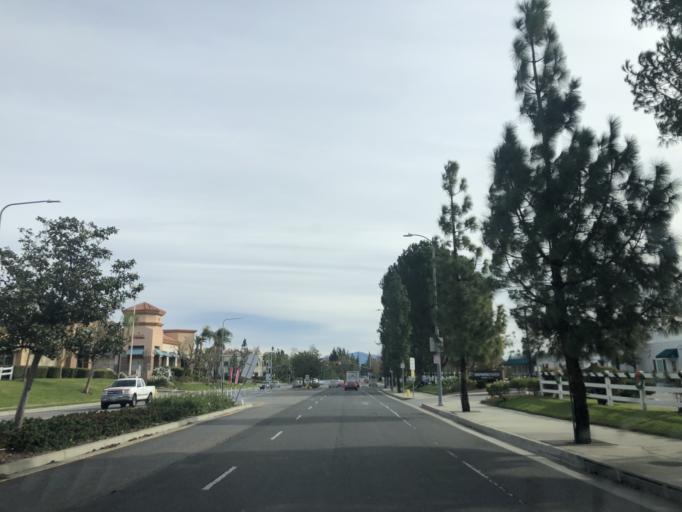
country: US
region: California
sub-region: Los Angeles County
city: Chatsworth
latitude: 34.2748
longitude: -118.5642
